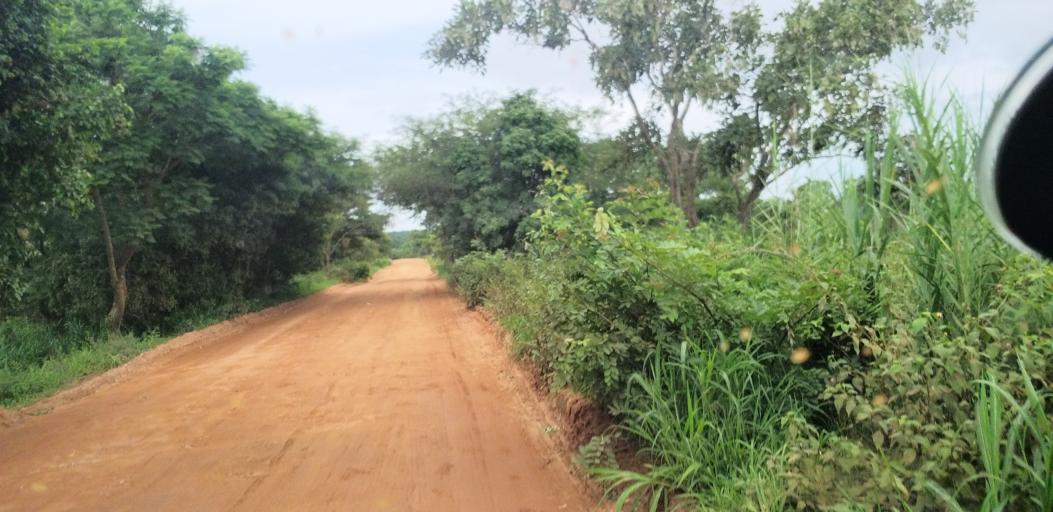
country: ZM
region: Lusaka
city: Lusaka
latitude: -15.1946
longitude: 28.4438
